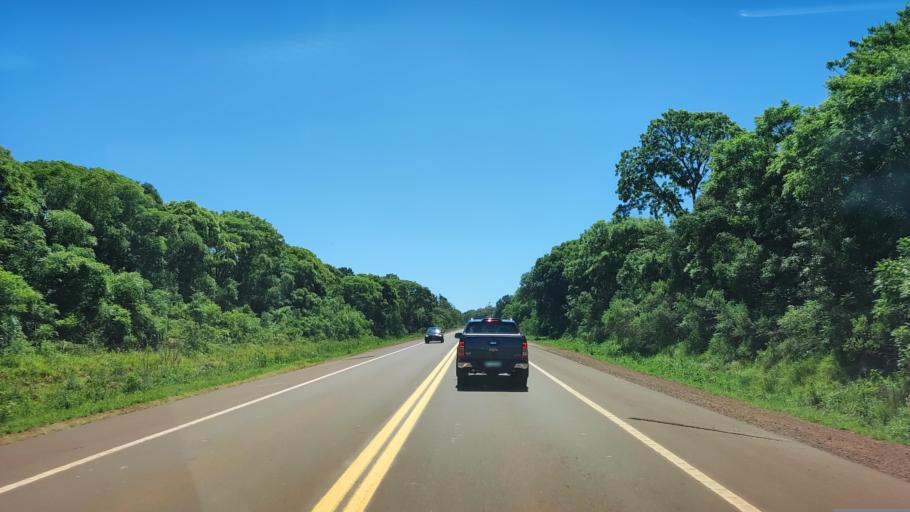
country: AR
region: Misiones
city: Dos de Mayo
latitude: -27.0850
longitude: -54.7774
